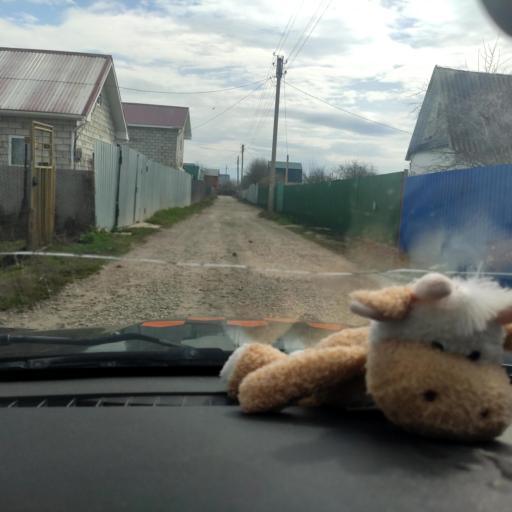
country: RU
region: Samara
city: Tol'yatti
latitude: 53.5973
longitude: 49.2405
